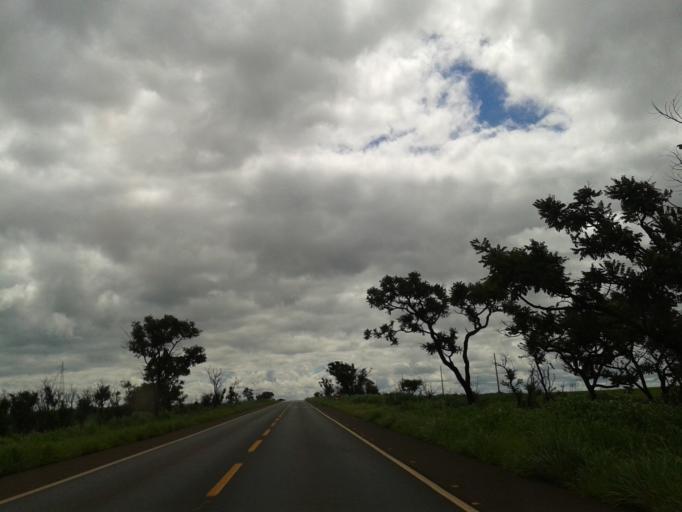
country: BR
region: Minas Gerais
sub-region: Ituiutaba
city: Ituiutaba
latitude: -18.8901
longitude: -49.2301
